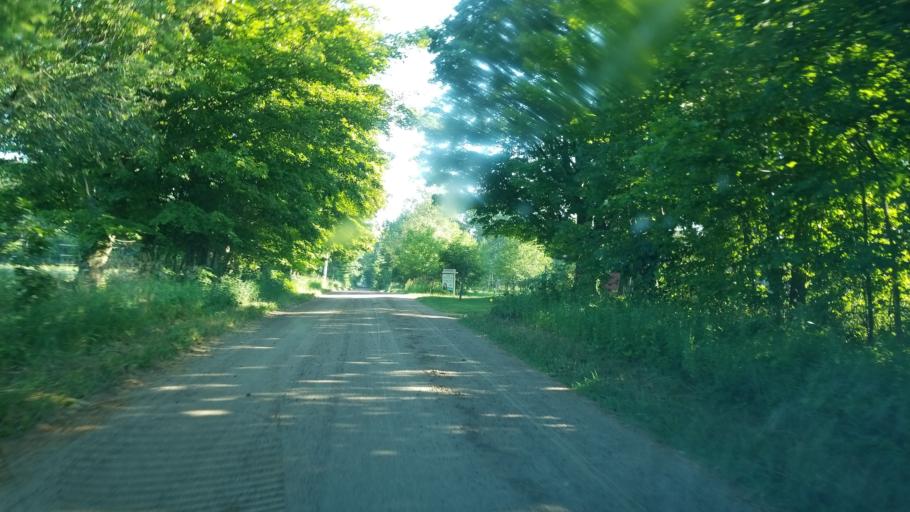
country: US
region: Michigan
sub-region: Mecosta County
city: Canadian Lakes
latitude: 43.5431
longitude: -85.4225
